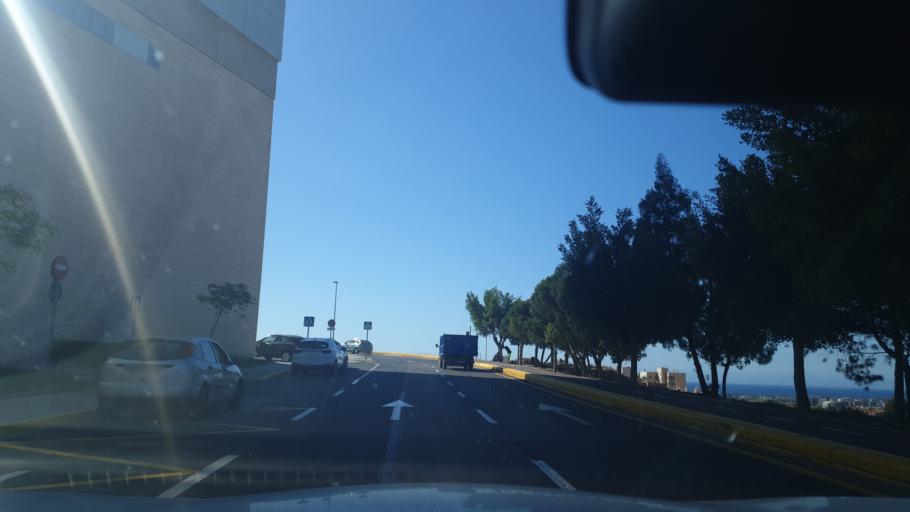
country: ES
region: Andalusia
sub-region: Provincia de Almeria
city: Huercal de Almeria
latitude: 36.8623
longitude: -2.4427
